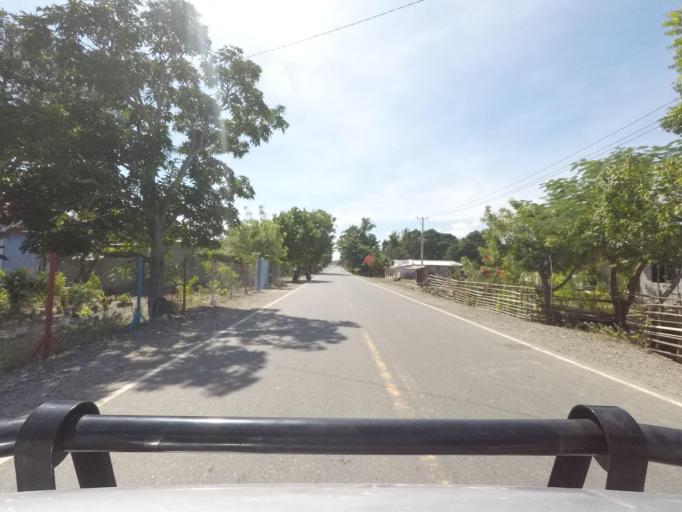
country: TL
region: Liquica
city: Maubara
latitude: -8.7878
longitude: 125.1015
